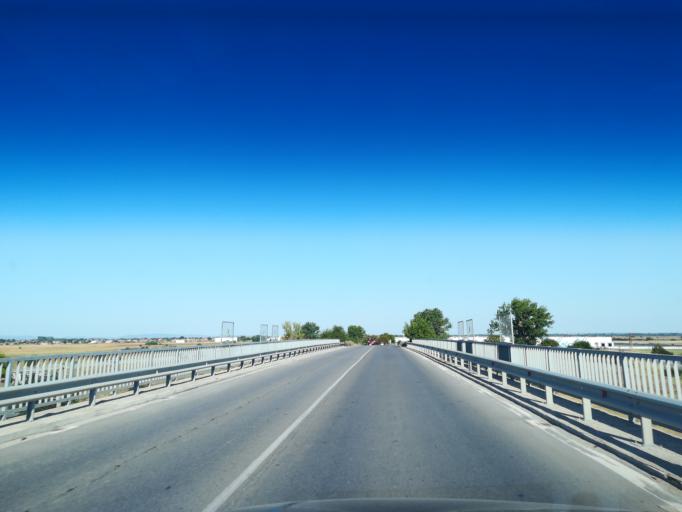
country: BG
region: Plovdiv
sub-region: Obshtina Plovdiv
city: Plovdiv
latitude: 42.1729
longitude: 24.8191
